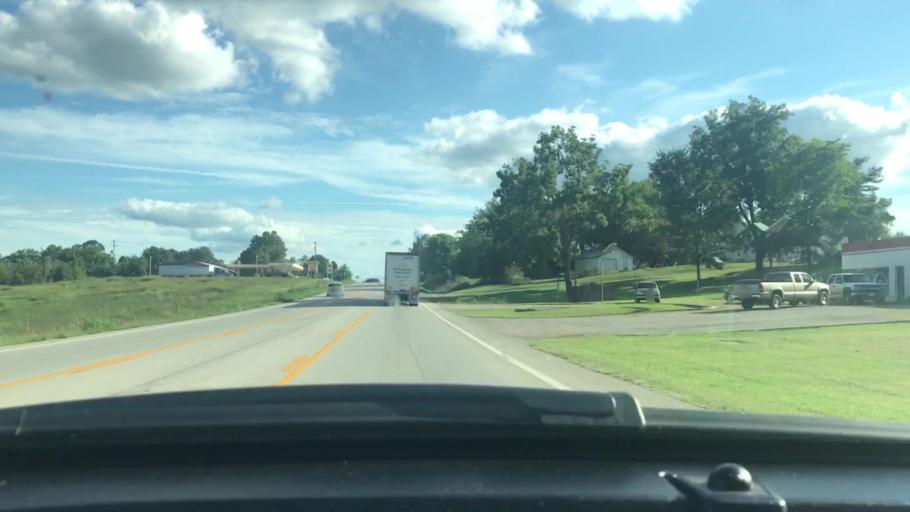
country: US
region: Missouri
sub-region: Oregon County
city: Thayer
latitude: 36.5972
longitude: -91.6440
